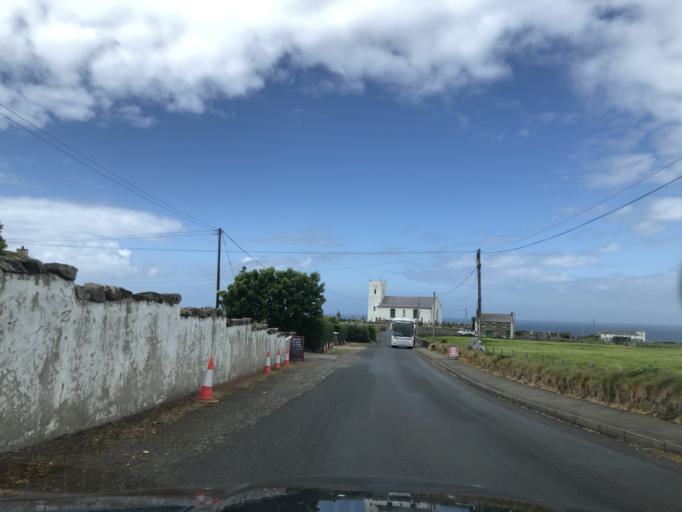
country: GB
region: Northern Ireland
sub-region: Moyle District
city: Ballycastle
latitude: 55.2387
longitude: -6.3658
